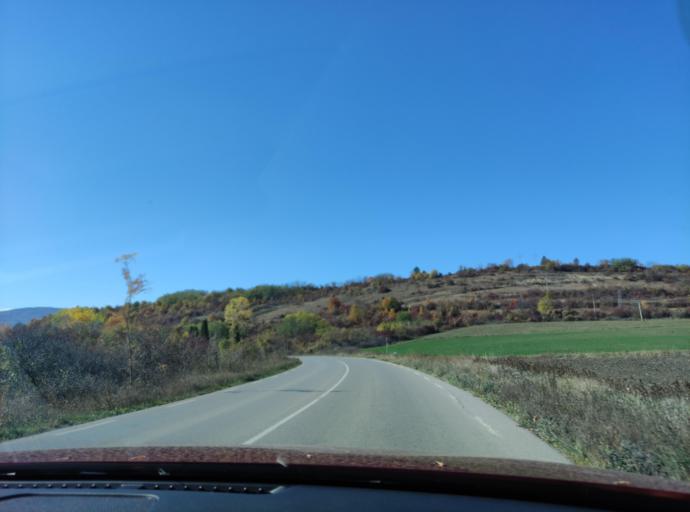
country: BG
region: Montana
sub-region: Obshtina Montana
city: Montana
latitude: 43.4010
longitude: 23.1321
